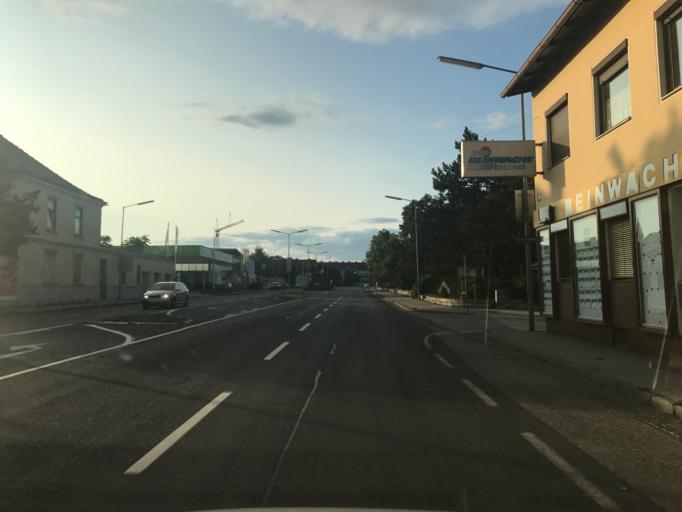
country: AT
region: Lower Austria
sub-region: Wiener Neustadt Stadt
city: Wiener Neustadt
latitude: 47.8239
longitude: 16.2457
